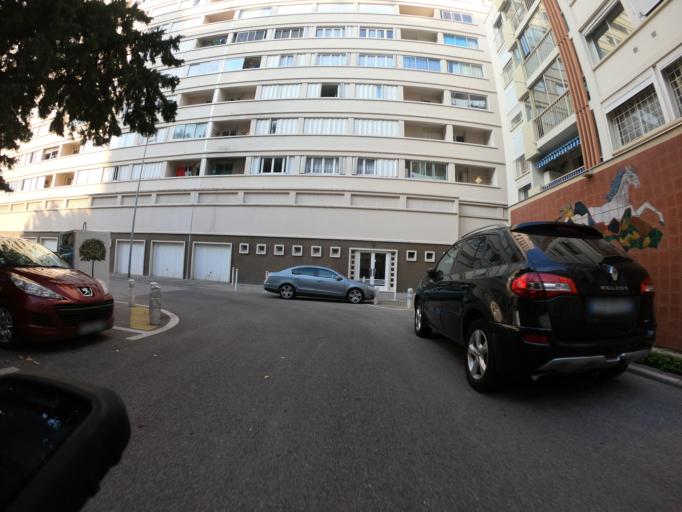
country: FR
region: Provence-Alpes-Cote d'Azur
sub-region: Departement du Var
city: Toulon
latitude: 43.1143
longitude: 5.9374
